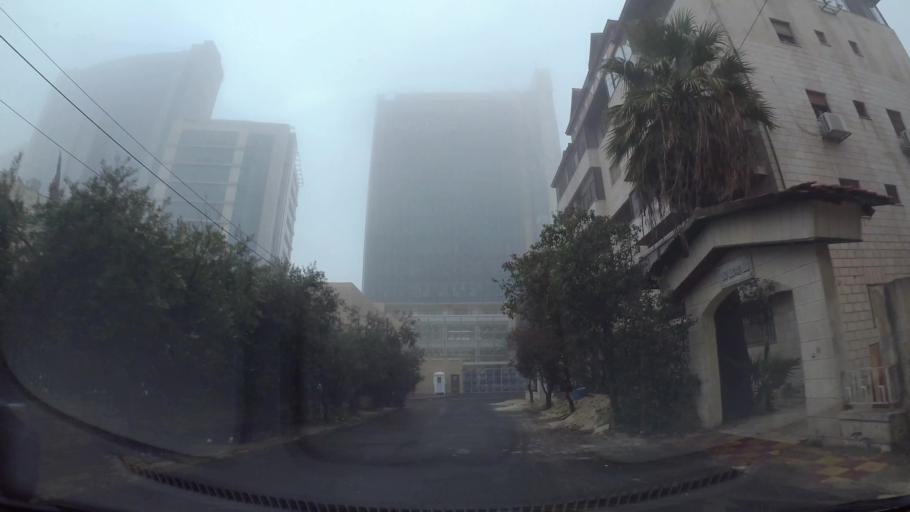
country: JO
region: Amman
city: Wadi as Sir
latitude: 31.9616
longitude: 35.8731
